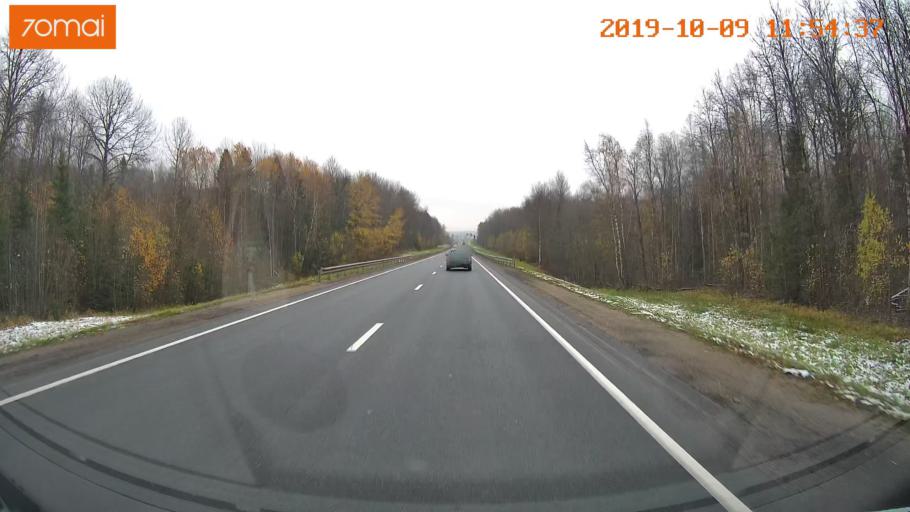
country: RU
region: Vologda
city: Gryazovets
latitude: 58.7570
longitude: 40.2822
